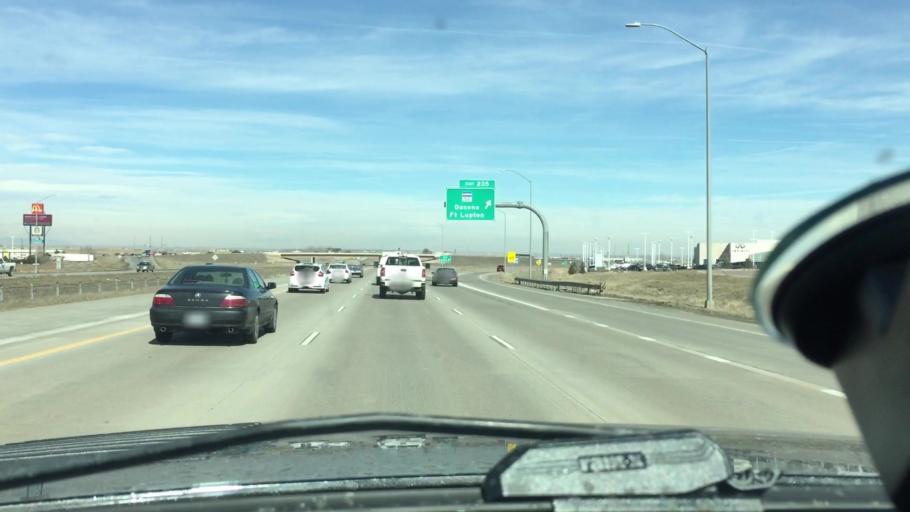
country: US
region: Colorado
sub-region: Weld County
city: Dacono
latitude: 40.0824
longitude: -104.9799
